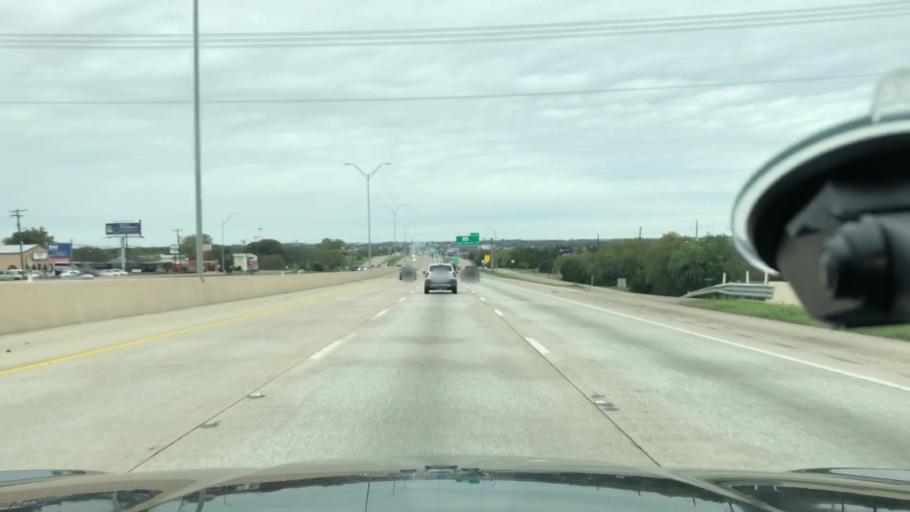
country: US
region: Texas
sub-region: Dallas County
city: DeSoto
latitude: 32.5767
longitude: -96.8223
